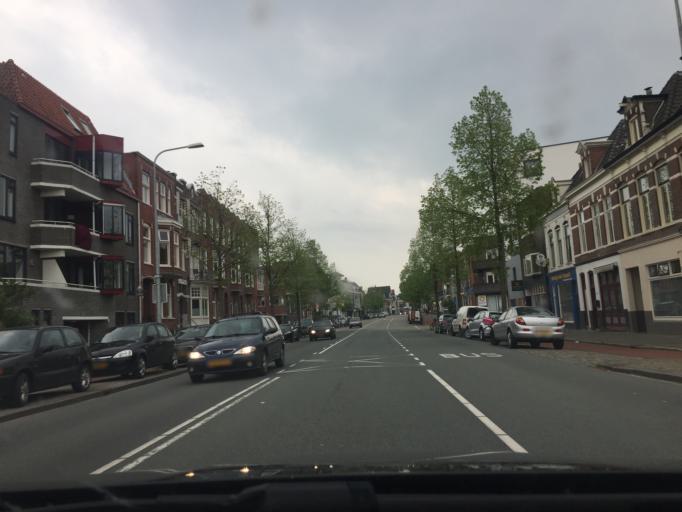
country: NL
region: Groningen
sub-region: Gemeente Groningen
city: Groningen
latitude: 53.2010
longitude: 6.5777
